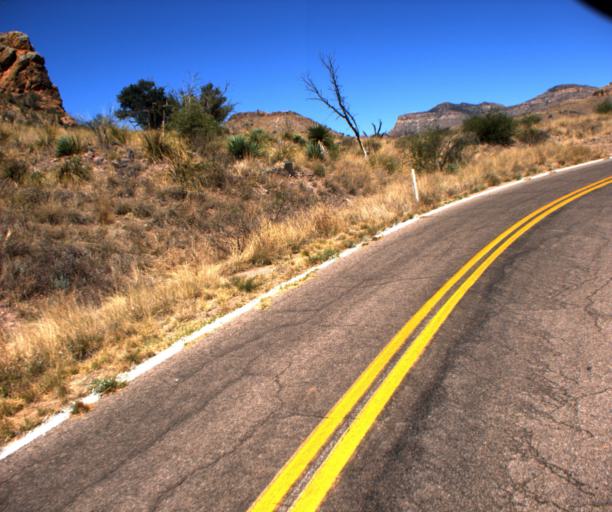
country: US
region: Arizona
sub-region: Santa Cruz County
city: Rio Rico
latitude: 31.3989
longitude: -111.0917
